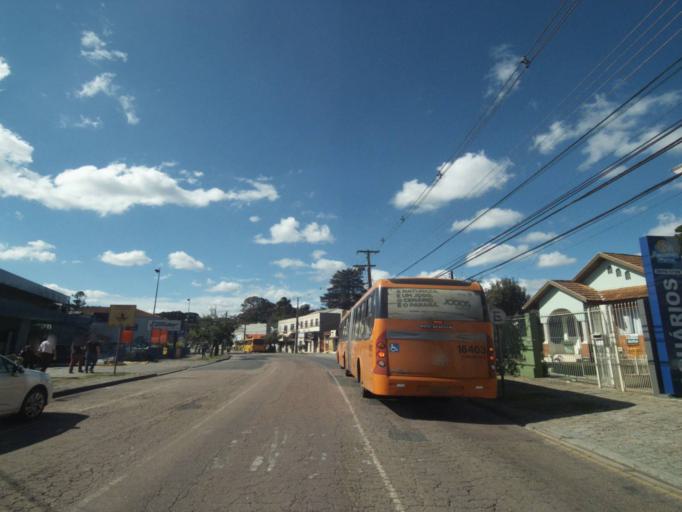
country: BR
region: Parana
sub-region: Curitiba
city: Curitiba
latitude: -25.3975
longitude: -49.2568
